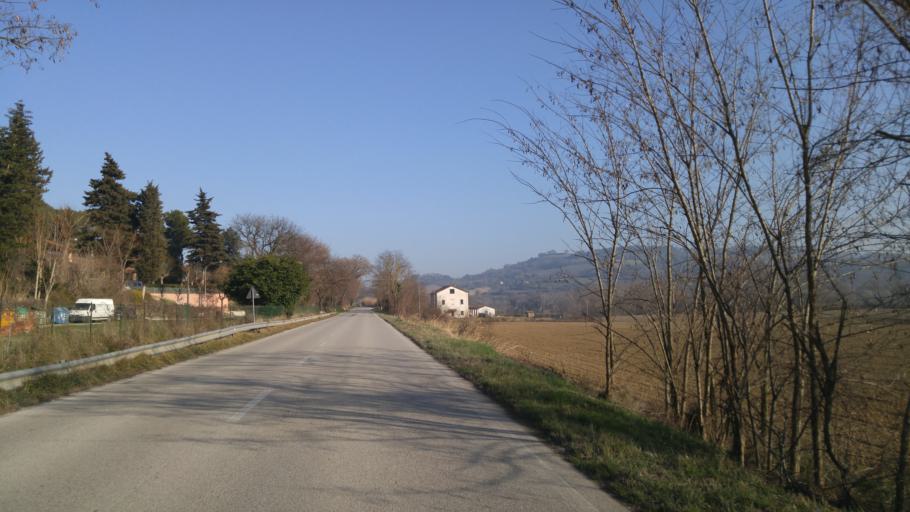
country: IT
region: The Marches
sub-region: Provincia di Pesaro e Urbino
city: Fenile
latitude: 43.8371
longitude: 12.9452
